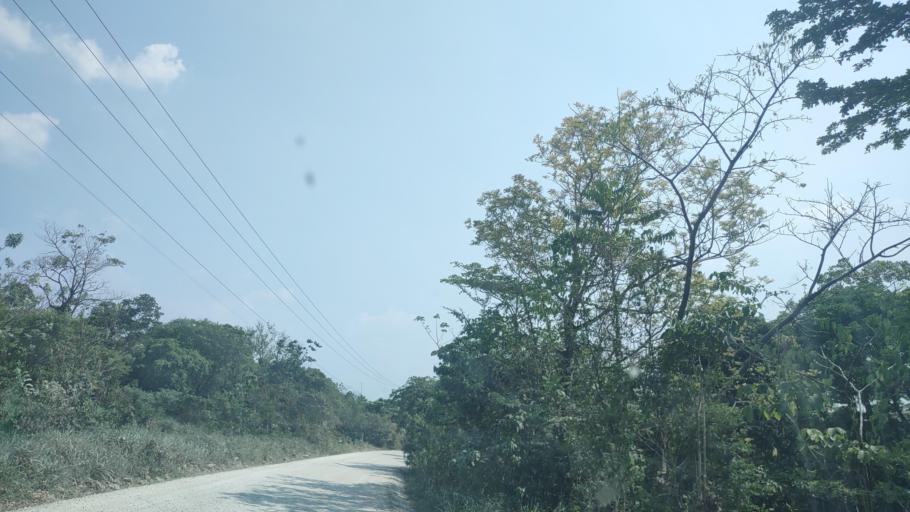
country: MX
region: Tabasco
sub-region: Huimanguillo
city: Francisco Rueda
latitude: 17.5684
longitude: -93.8861
